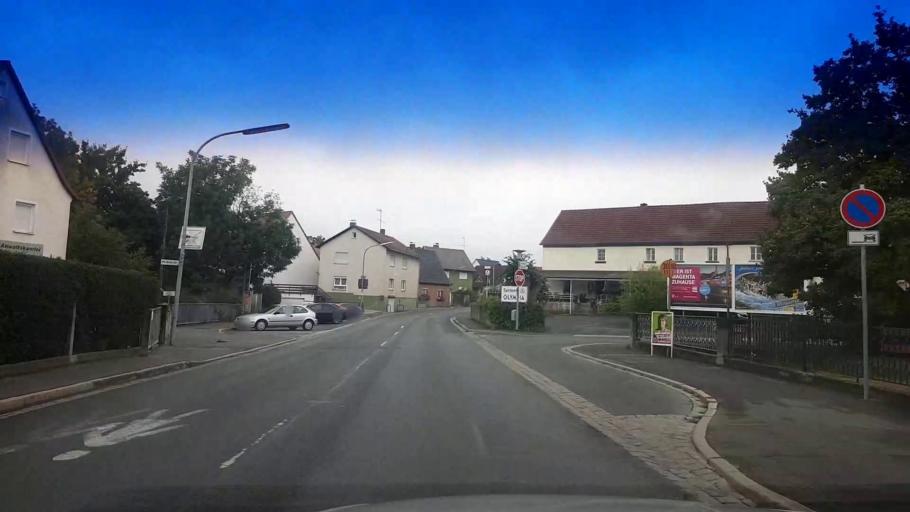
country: DE
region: Bavaria
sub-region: Upper Franconia
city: Forchheim
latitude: 49.7189
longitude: 11.0426
